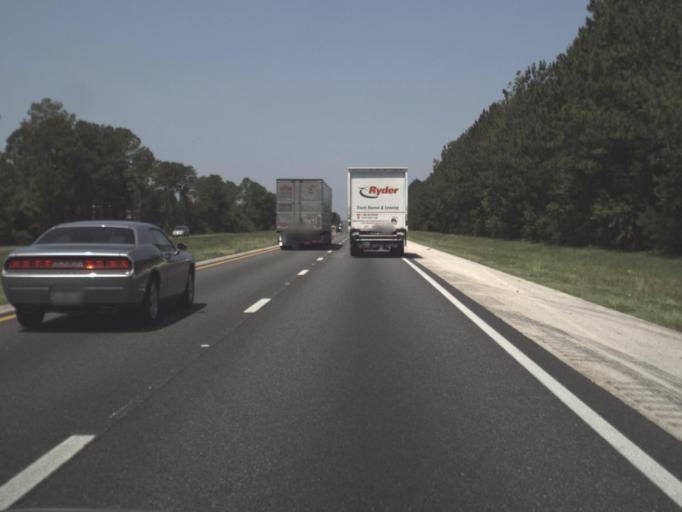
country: US
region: Florida
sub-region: Duval County
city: Baldwin
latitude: 30.3041
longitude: -81.9033
